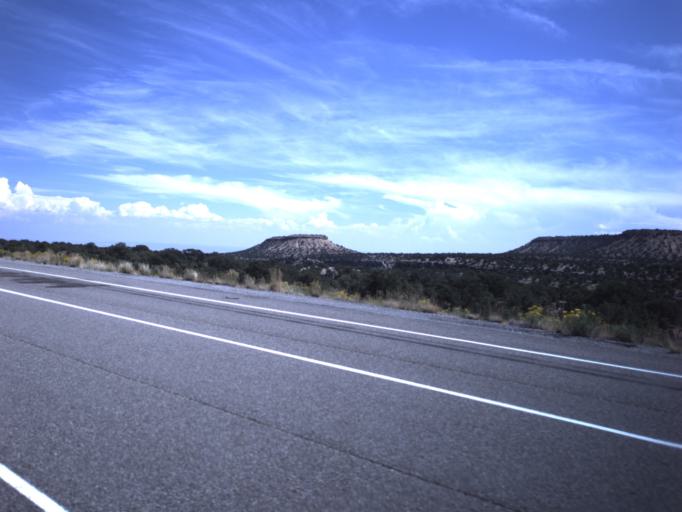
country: US
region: Utah
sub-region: Emery County
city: Castle Dale
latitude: 38.9045
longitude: -110.5390
